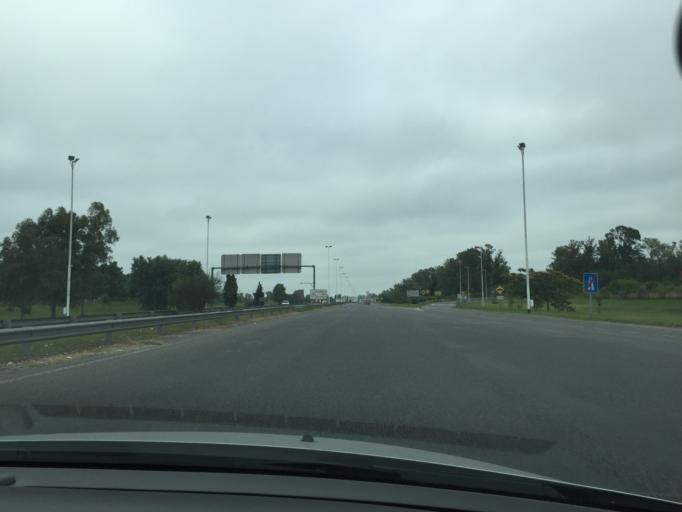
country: AR
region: Buenos Aires
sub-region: Partido de Ezeiza
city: Ezeiza
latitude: -34.8552
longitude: -58.5540
